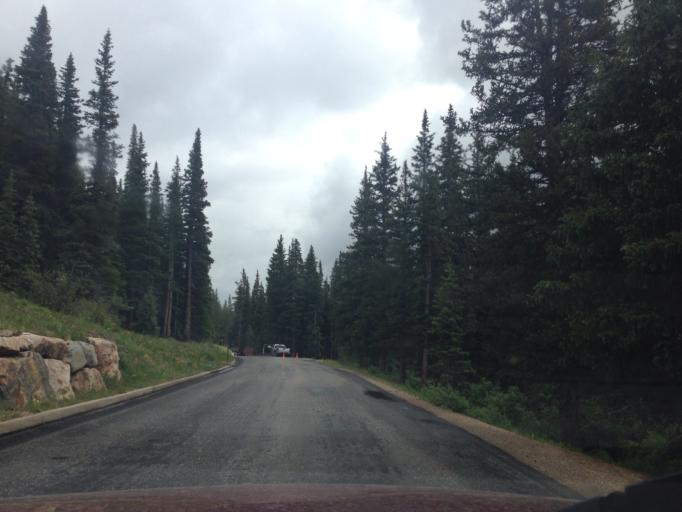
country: US
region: Colorado
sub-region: Clear Creek County
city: Georgetown
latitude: 39.6144
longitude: -105.7165
